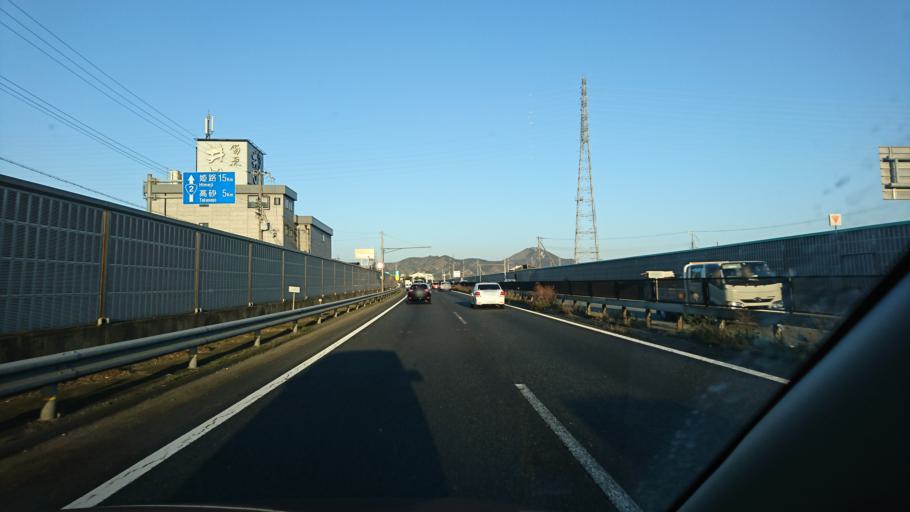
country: JP
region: Hyogo
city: Kakogawacho-honmachi
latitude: 34.7838
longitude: 134.8288
